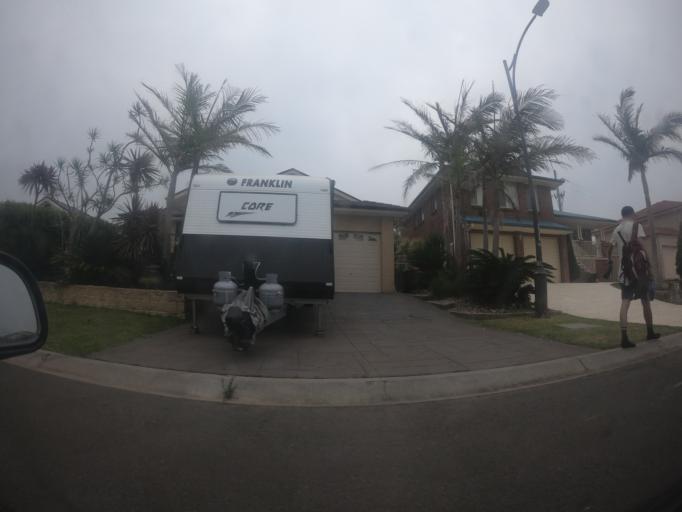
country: AU
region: New South Wales
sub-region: Shellharbour
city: Croom
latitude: -34.5927
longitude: 150.8491
